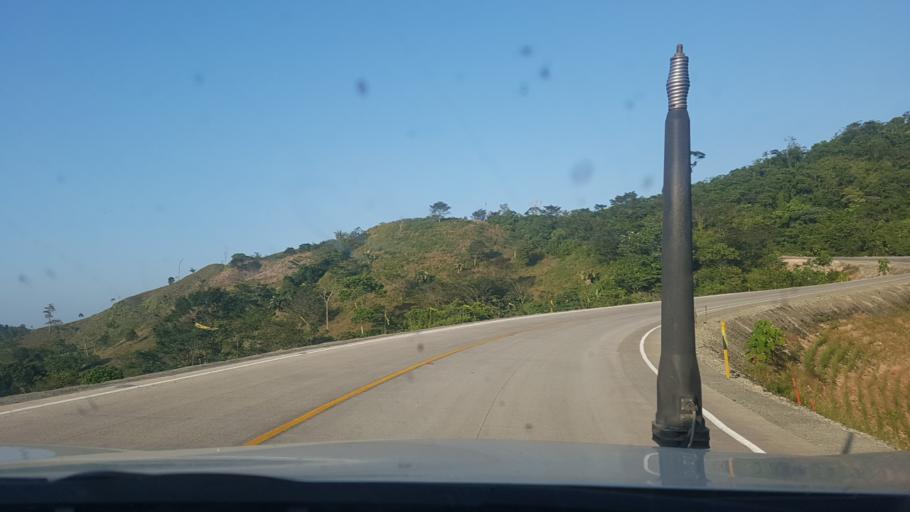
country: NI
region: Atlantico Sur
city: Rama
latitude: 11.8267
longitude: -84.0843
